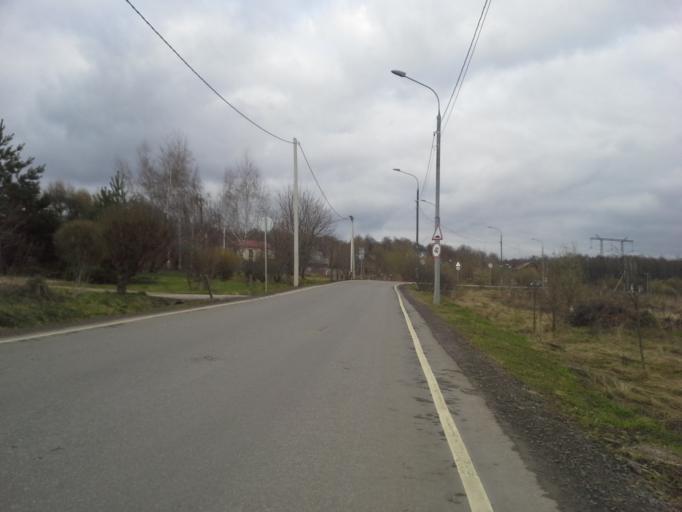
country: RU
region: Moskovskaya
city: Kommunarka
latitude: 55.5716
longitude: 37.5132
